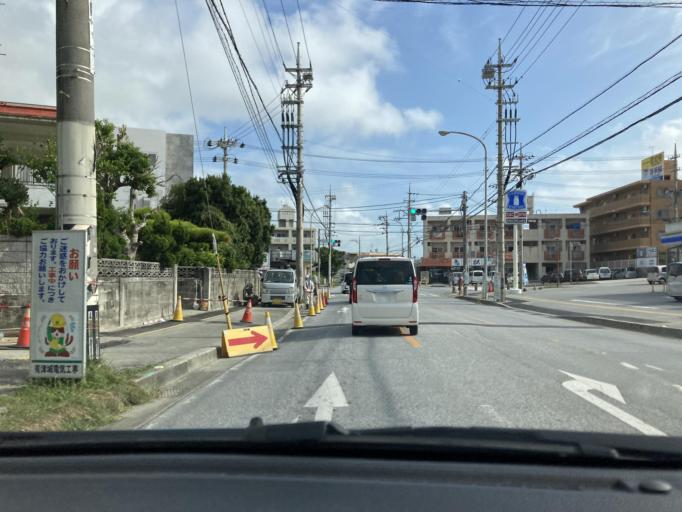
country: JP
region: Okinawa
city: Ginowan
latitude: 26.2539
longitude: 127.7739
